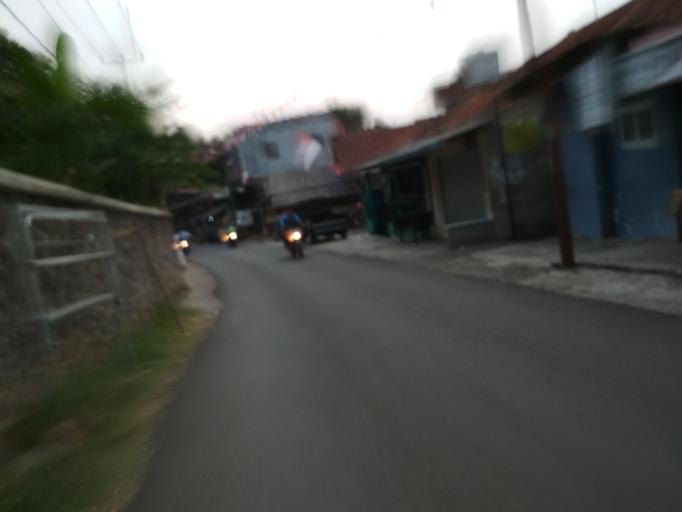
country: ID
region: West Java
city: Ciampea
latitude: -6.5563
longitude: 106.7349
